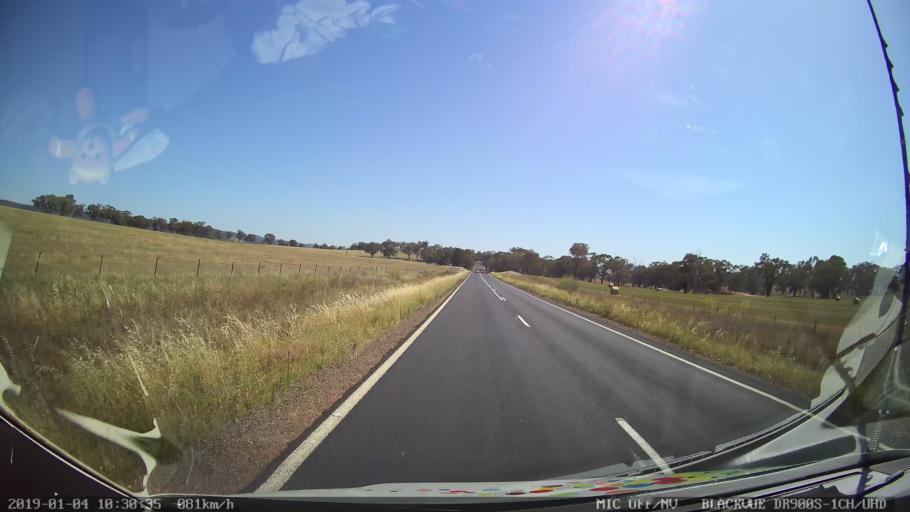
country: AU
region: New South Wales
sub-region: Cabonne
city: Canowindra
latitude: -33.3442
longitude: 148.6286
